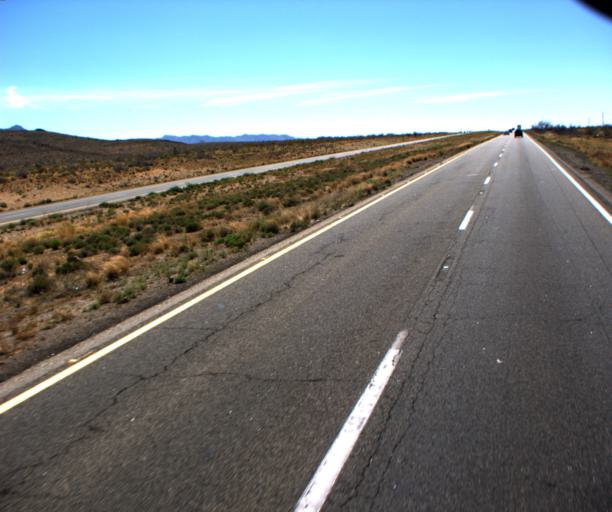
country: US
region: Arizona
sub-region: Mohave County
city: Dolan Springs
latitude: 35.4291
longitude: -114.2829
